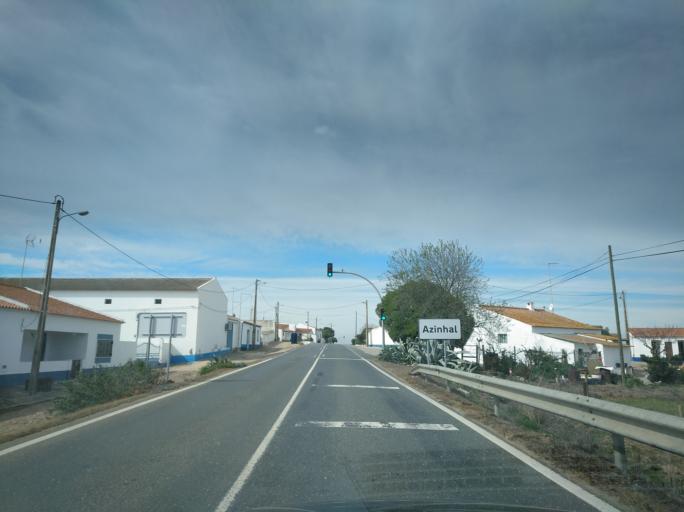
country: PT
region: Beja
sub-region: Mertola
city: Mertola
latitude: 37.7604
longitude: -7.8138
